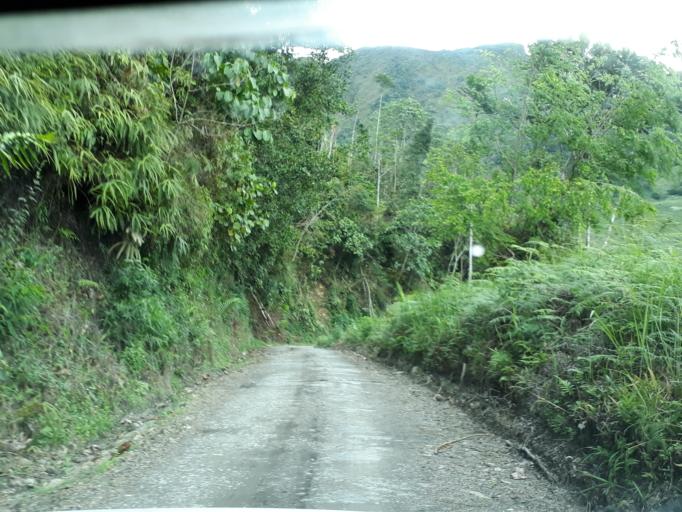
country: CO
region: Boyaca
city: Quipama
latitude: 5.4162
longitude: -74.1888
